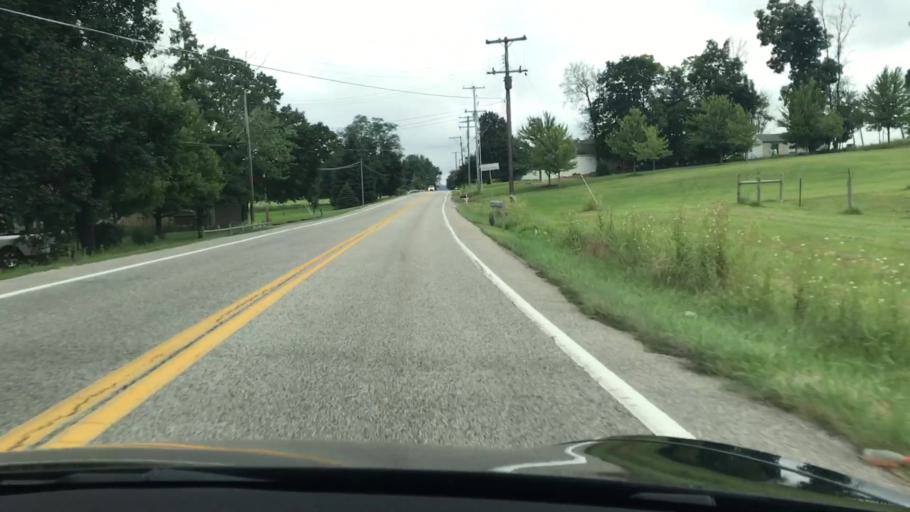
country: US
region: Pennsylvania
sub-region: Cumberland County
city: Shiremanstown
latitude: 40.1535
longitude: -76.9669
